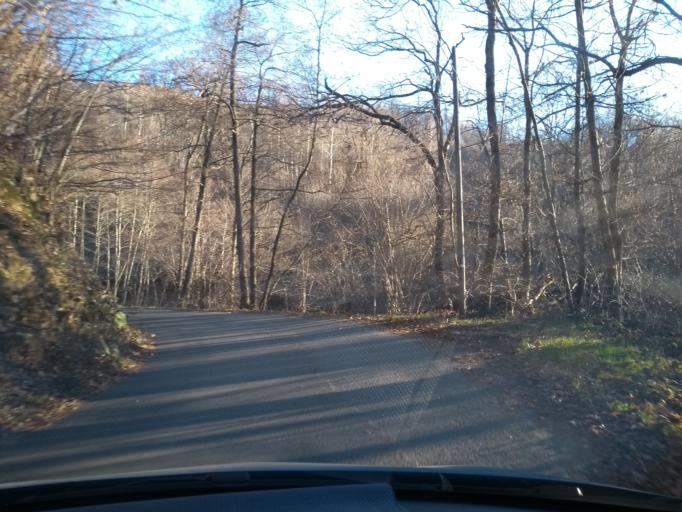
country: IT
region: Piedmont
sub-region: Provincia di Torino
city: Corio
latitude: 45.3236
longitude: 7.5388
